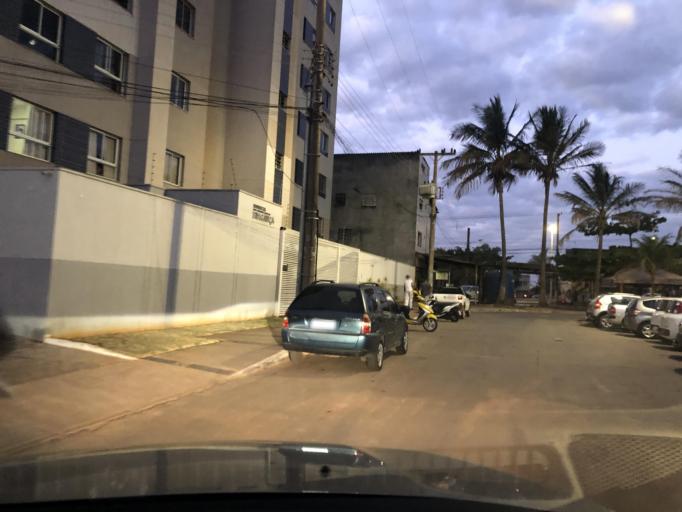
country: BR
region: Federal District
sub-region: Brasilia
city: Brasilia
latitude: -15.8510
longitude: -48.0739
